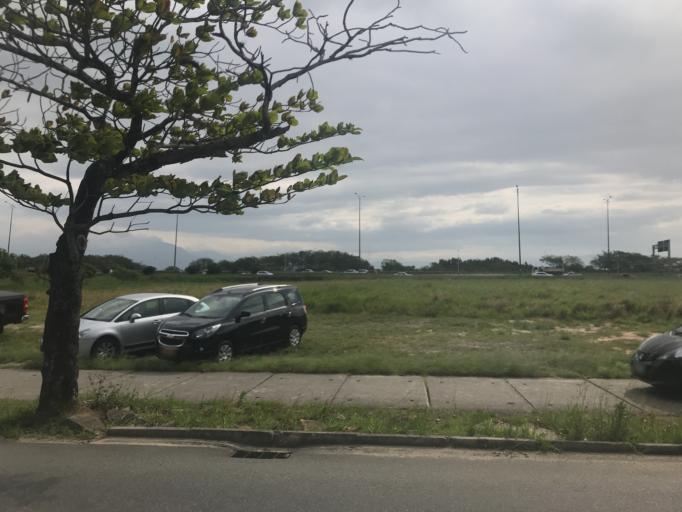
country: BR
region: Santa Catarina
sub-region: Florianopolis
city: Pantanal
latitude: -27.6212
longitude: -48.5266
